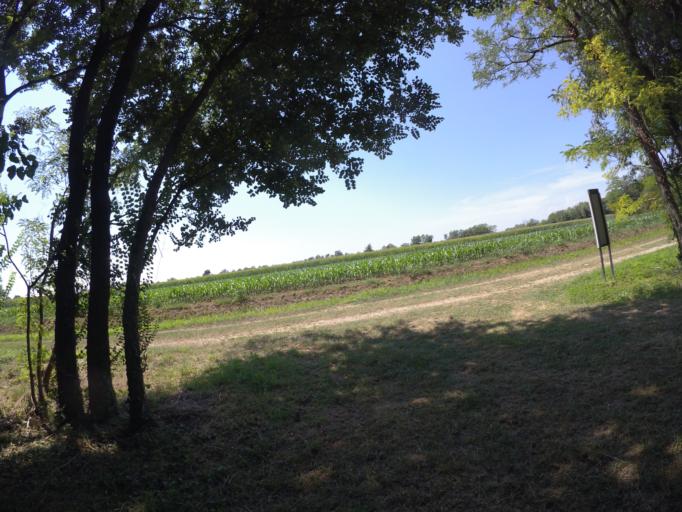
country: IT
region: Friuli Venezia Giulia
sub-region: Provincia di Udine
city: Mortegliano
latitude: 45.9323
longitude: 13.1813
